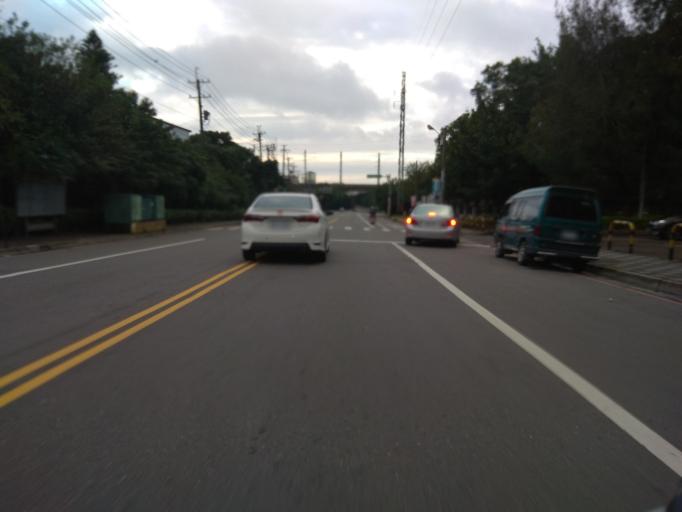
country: TW
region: Taiwan
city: Daxi
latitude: 24.9255
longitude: 121.1759
